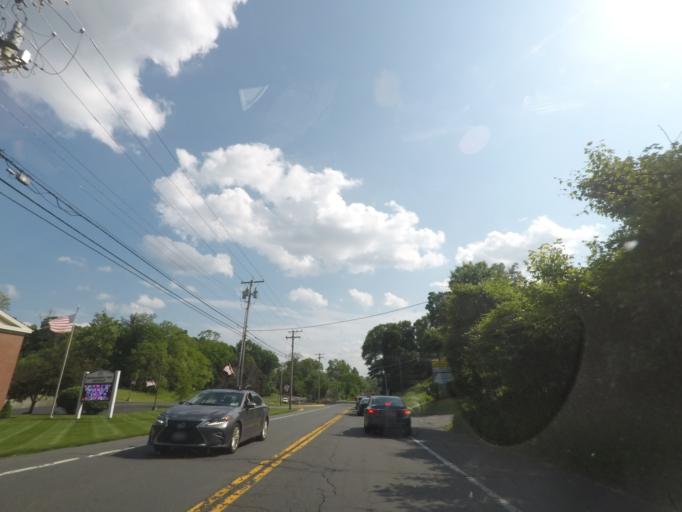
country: US
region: New York
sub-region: Orange County
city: Balmville
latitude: 41.5378
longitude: -74.0132
